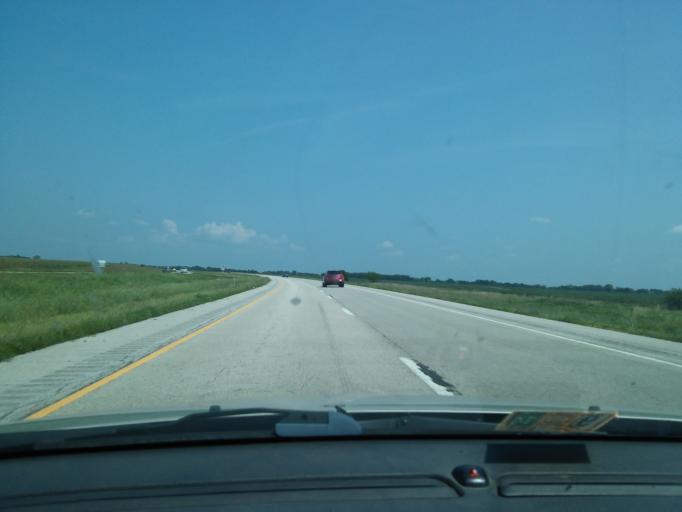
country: US
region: Illinois
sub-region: Sangamon County
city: New Berlin
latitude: 39.7369
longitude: -89.9843
